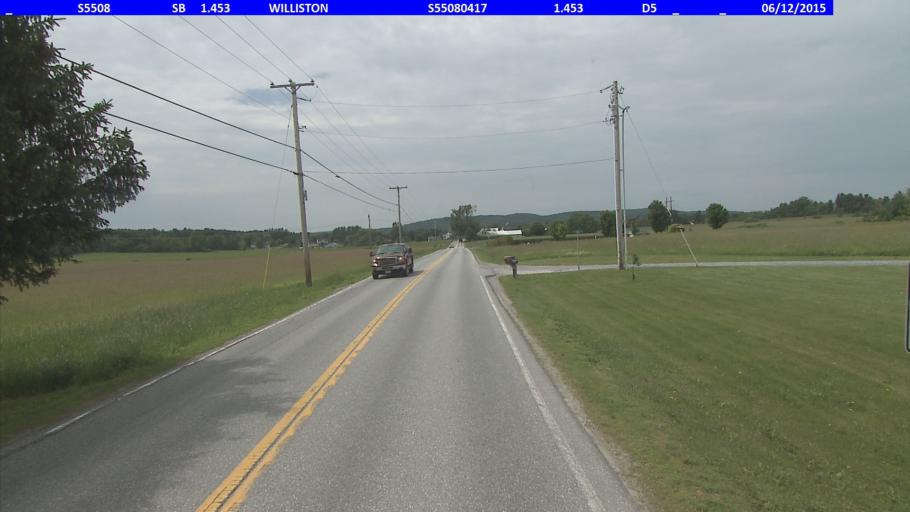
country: US
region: Vermont
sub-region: Chittenden County
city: Williston
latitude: 44.4559
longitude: -73.0550
